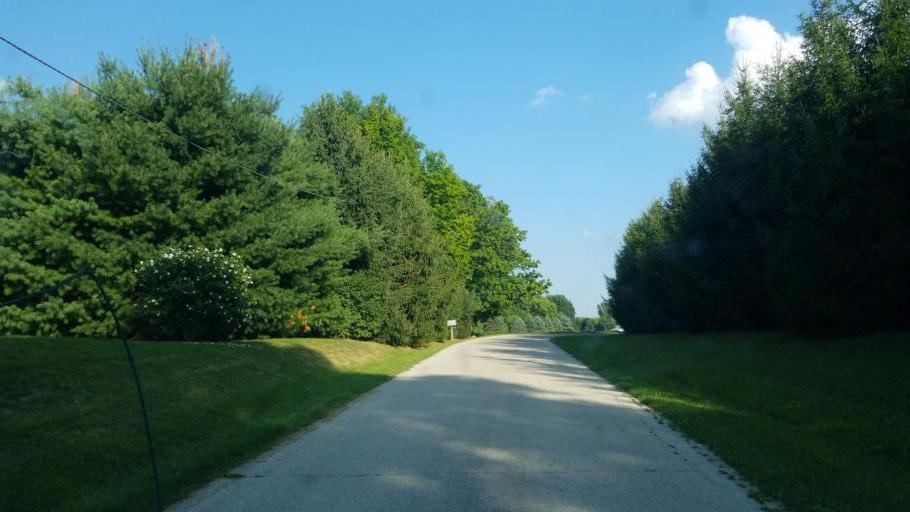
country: US
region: Ohio
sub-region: Crawford County
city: Bucyrus
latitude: 40.8316
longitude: -82.8976
